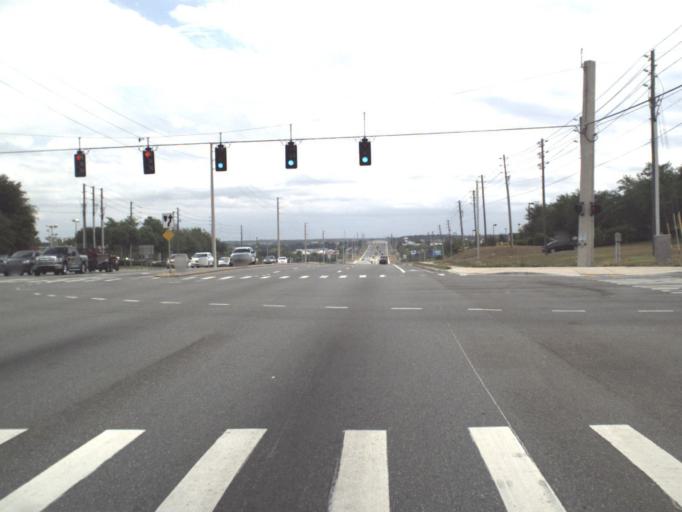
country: US
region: Florida
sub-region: Lake County
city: Minneola
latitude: 28.5466
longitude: -81.7072
